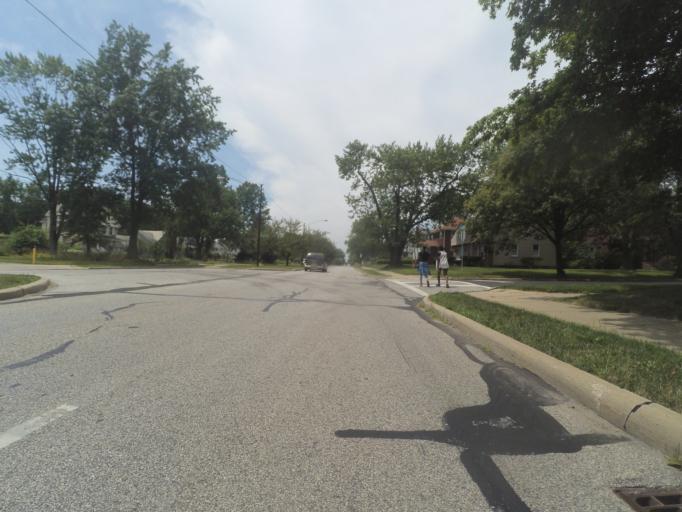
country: US
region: Ohio
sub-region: Cuyahoga County
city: University Heights
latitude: 41.4866
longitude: -81.5507
